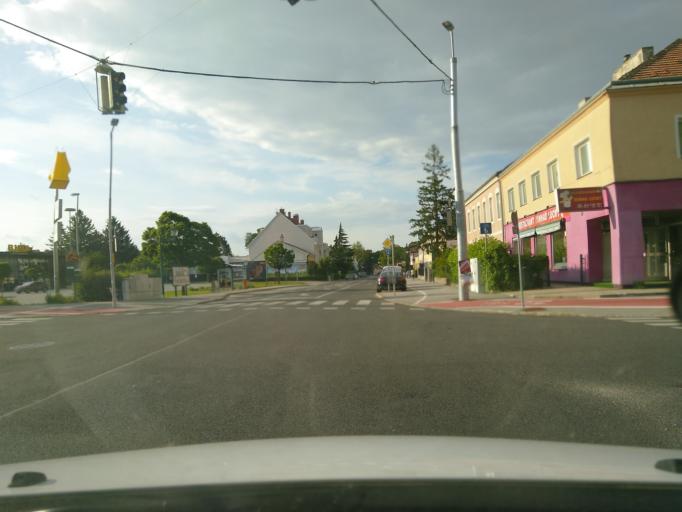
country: AT
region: Lower Austria
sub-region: Politischer Bezirk Modling
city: Maria Enzersdorf
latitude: 48.0933
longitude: 16.2837
